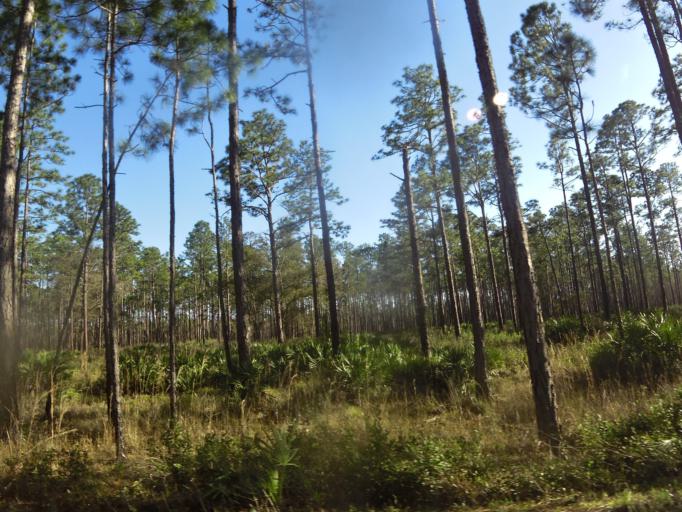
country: US
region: Florida
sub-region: Clay County
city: Middleburg
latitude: 30.1482
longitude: -81.8959
